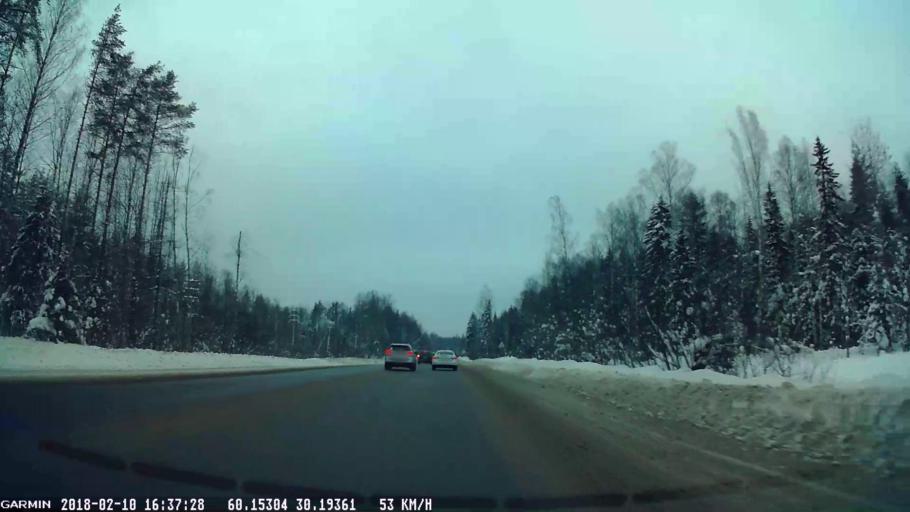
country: RU
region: Leningrad
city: Sertolovo
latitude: 60.1503
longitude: 30.1970
